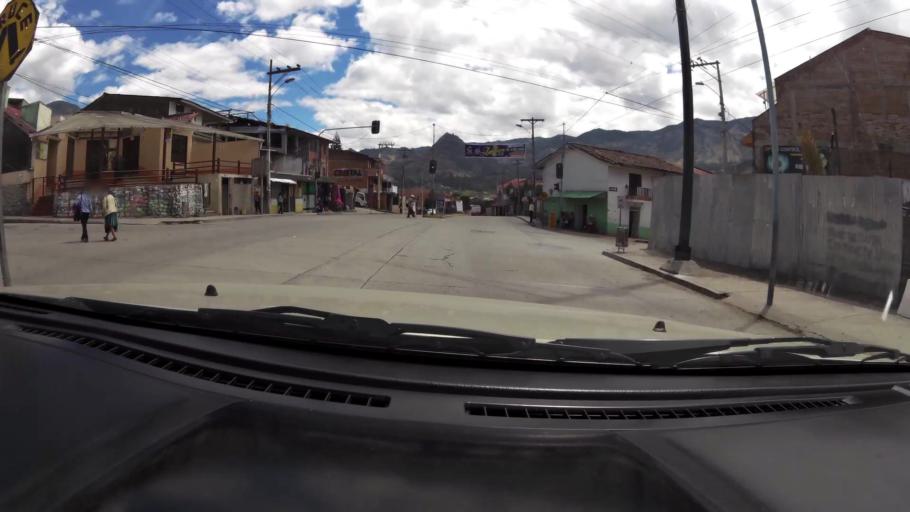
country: EC
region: Azuay
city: Cuenca
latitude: -3.1590
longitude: -79.1498
